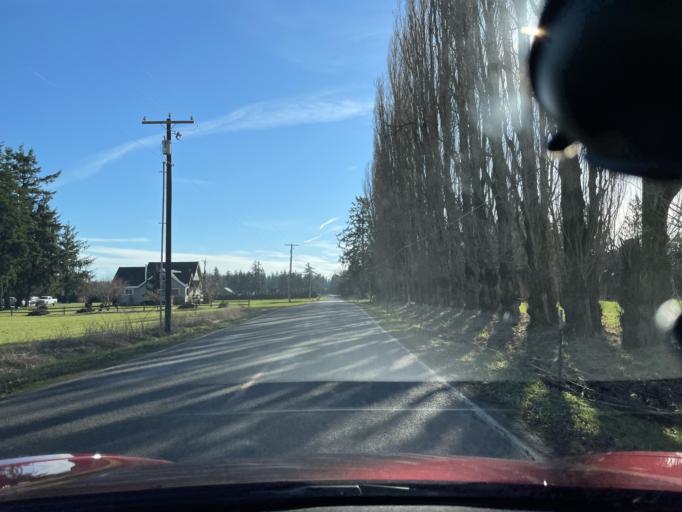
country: US
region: Washington
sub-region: Whatcom County
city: Lynden
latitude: 48.9805
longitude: -122.5129
